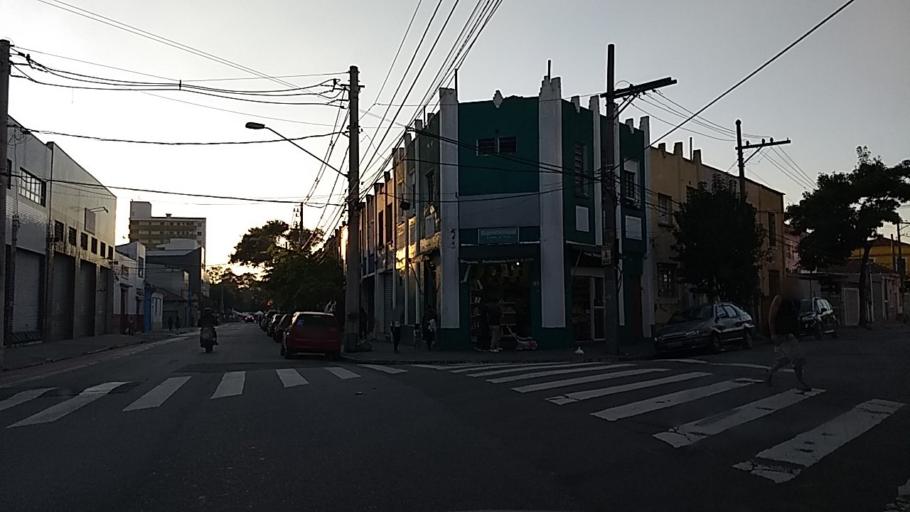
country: BR
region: Sao Paulo
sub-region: Sao Paulo
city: Sao Paulo
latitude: -23.5275
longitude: -46.6189
